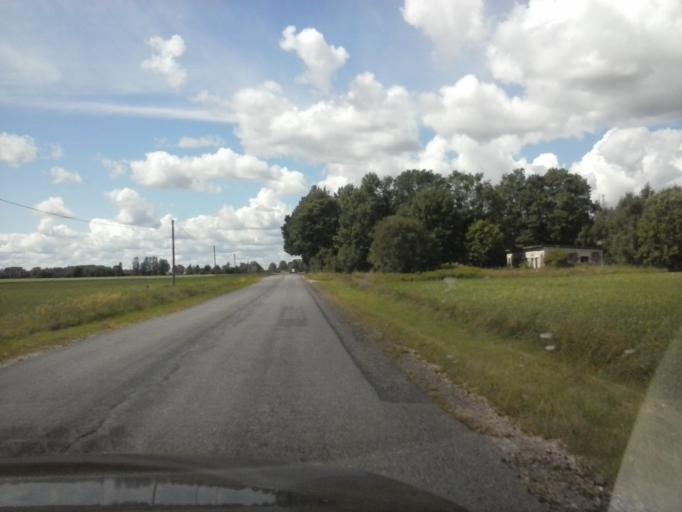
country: EE
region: Laeaene-Virumaa
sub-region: Rakke vald
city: Rakke
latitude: 59.0532
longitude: 26.3580
